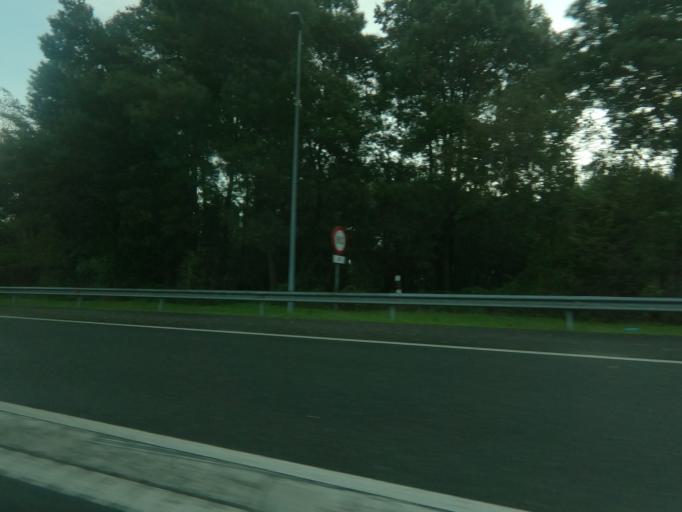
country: ES
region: Galicia
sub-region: Provincia de Pontevedra
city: Tui
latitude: 42.0522
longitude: -8.6550
